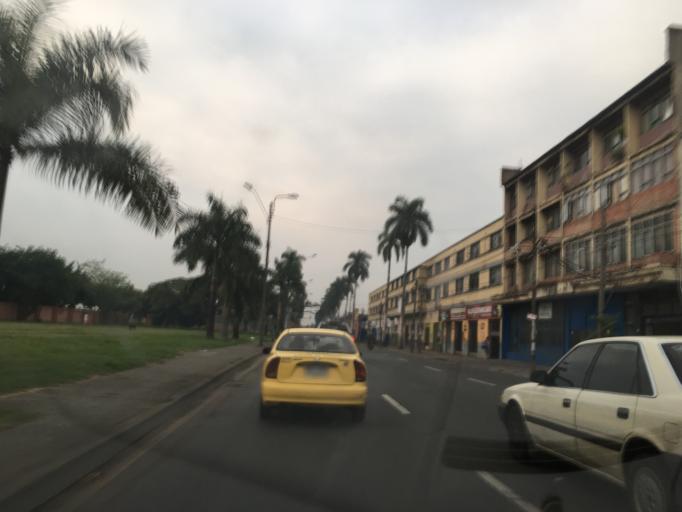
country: CO
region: Valle del Cauca
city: Cali
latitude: 3.4583
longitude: -76.5206
